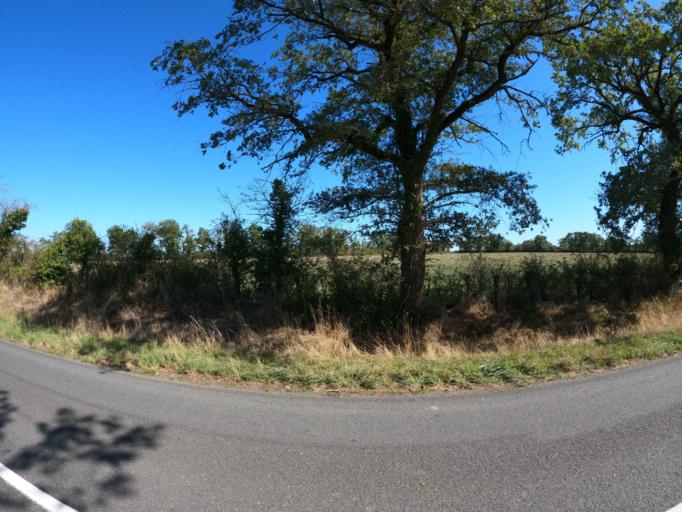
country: FR
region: Poitou-Charentes
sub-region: Departement de la Vienne
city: Lathus-Saint-Remy
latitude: 46.2987
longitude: 0.9951
